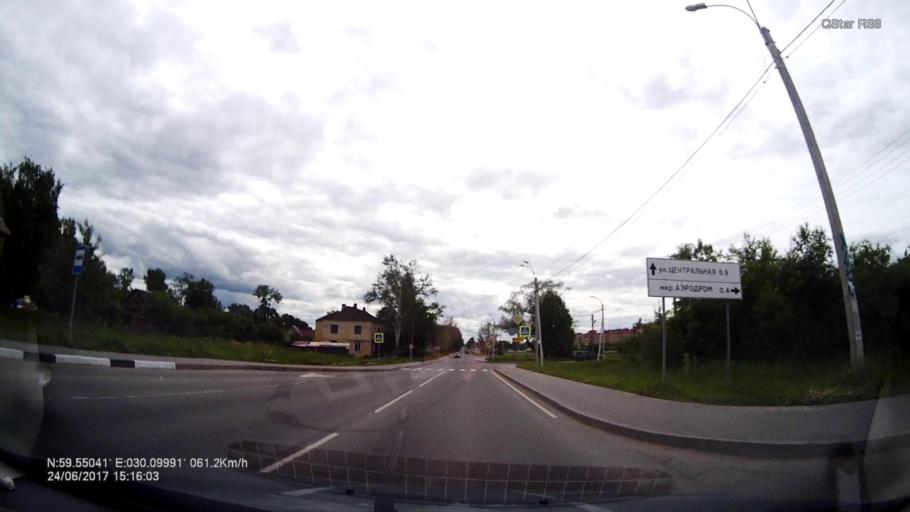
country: RU
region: Leningrad
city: Gatchina
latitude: 59.5504
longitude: 30.0998
